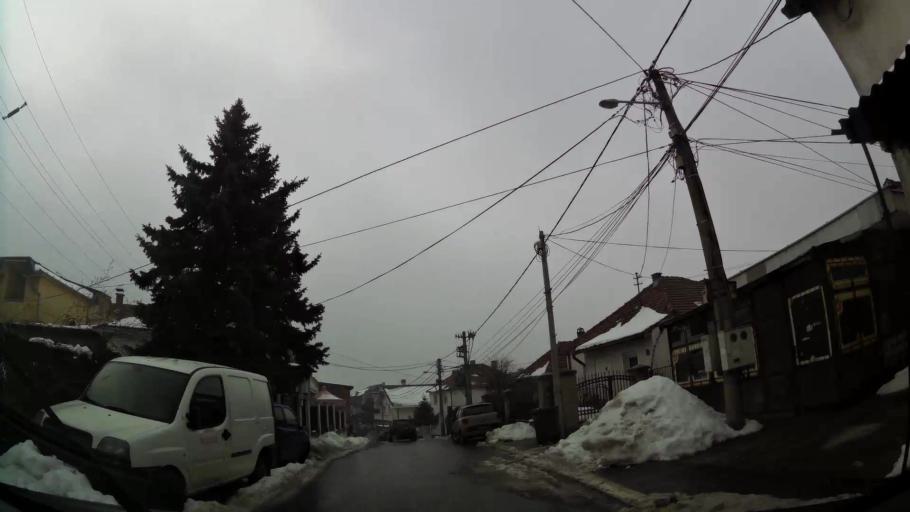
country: RS
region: Central Serbia
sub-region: Belgrade
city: Zvezdara
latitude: 44.7812
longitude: 20.5198
